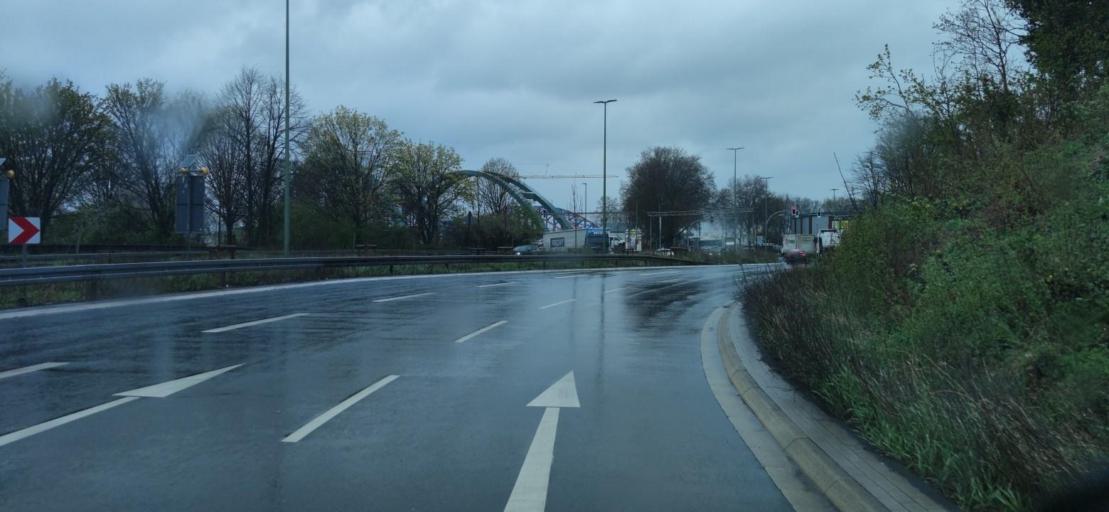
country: DE
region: North Rhine-Westphalia
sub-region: Regierungsbezirk Dusseldorf
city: Duisburg
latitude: 51.4405
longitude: 6.7453
